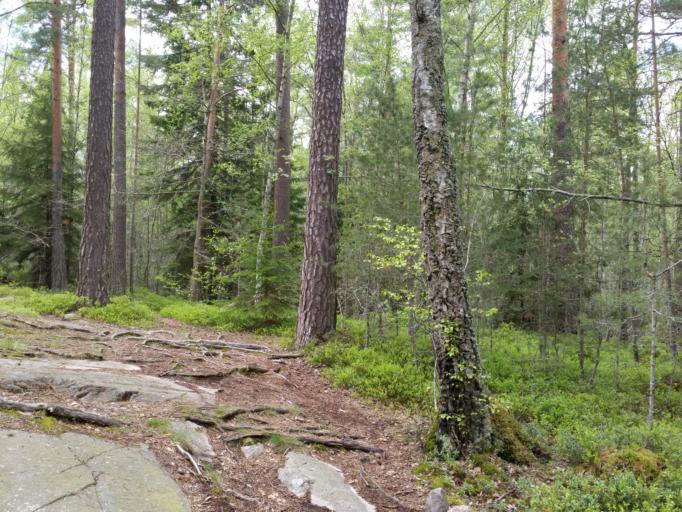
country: SE
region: Stockholm
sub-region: Sollentuna Kommun
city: Sollentuna
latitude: 59.4644
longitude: 17.9538
